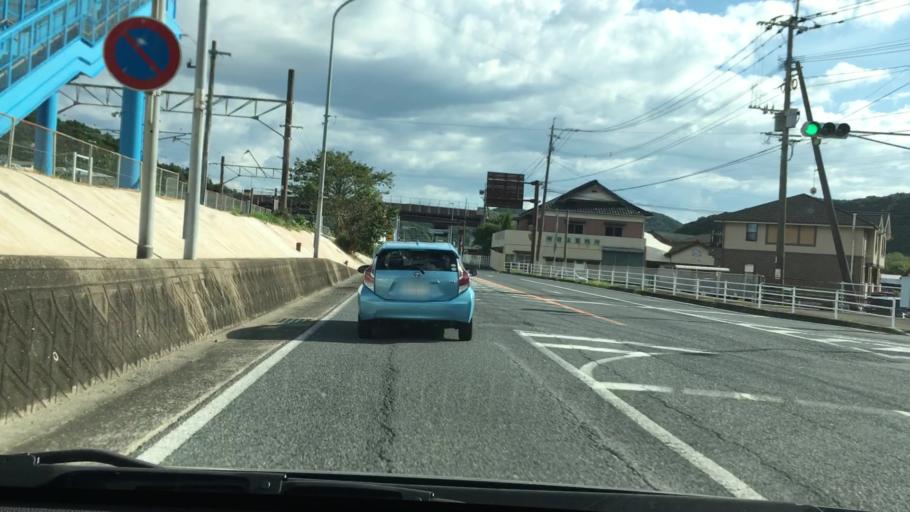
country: JP
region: Nagasaki
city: Sasebo
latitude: 33.1502
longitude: 129.8291
